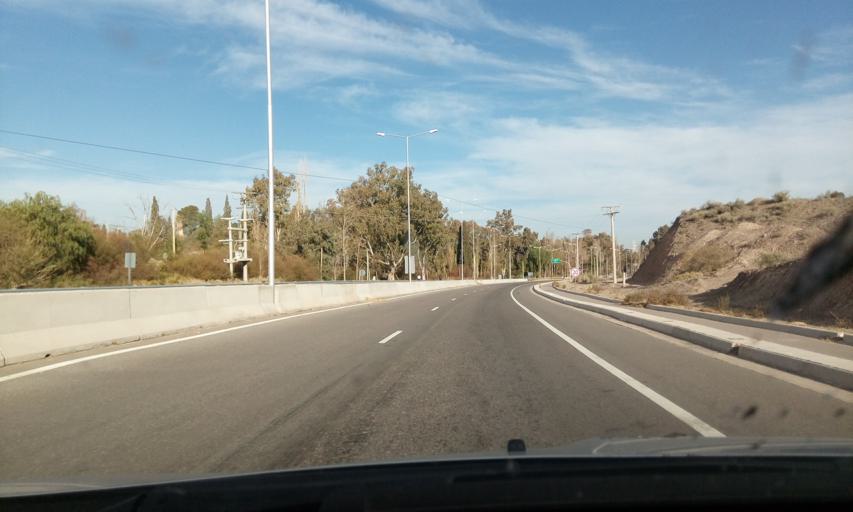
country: AR
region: San Juan
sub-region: Departamento de Rivadavia
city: Rivadavia
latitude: -31.5035
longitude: -68.6461
